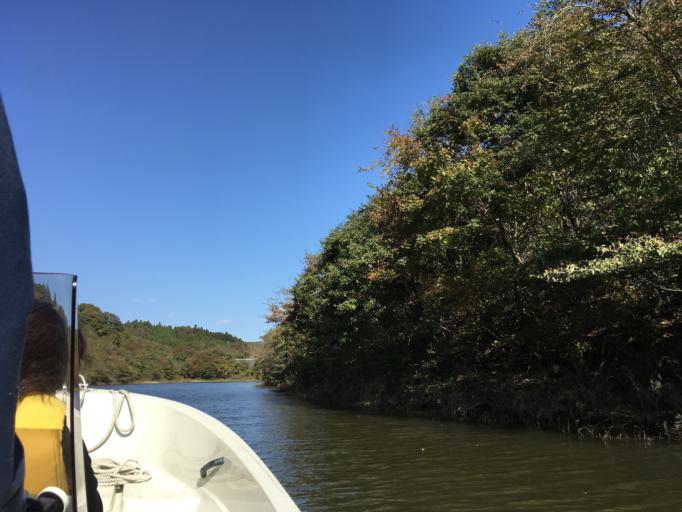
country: JP
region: Iwate
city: Ichinoseki
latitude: 38.7999
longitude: 141.2896
